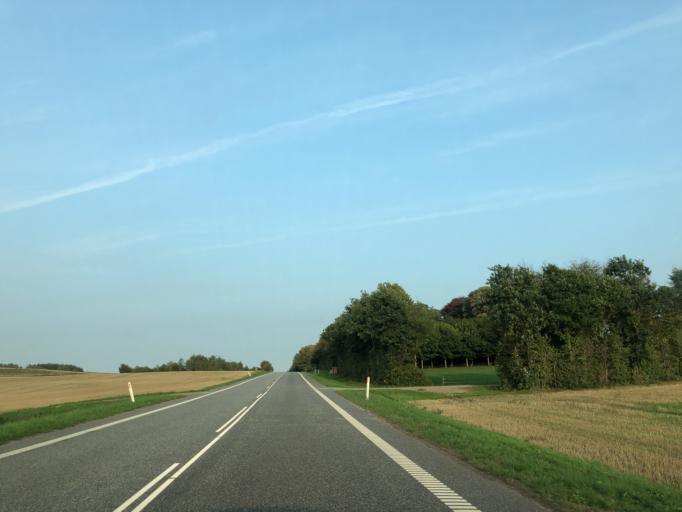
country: DK
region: South Denmark
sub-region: Vejle Kommune
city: Jelling
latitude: 55.7010
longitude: 9.3941
